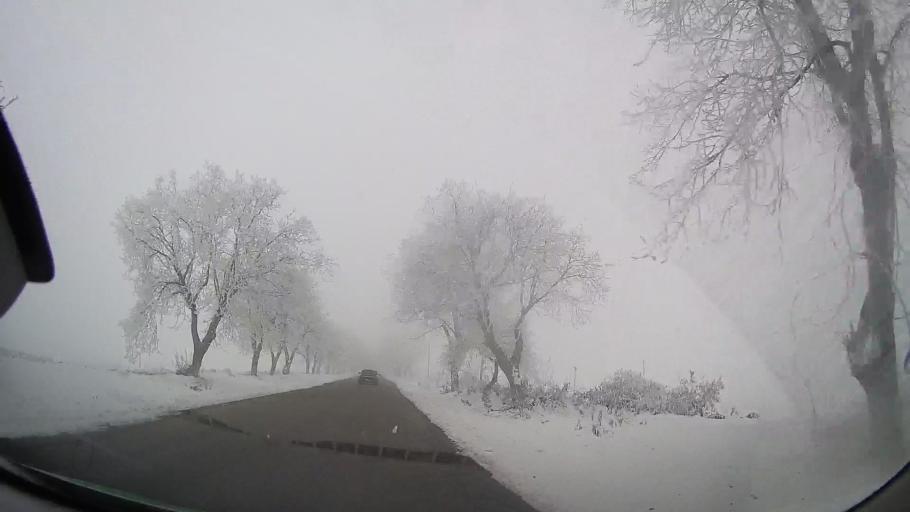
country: RO
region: Neamt
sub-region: Comuna Sabaoani
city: Sabaoani
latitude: 46.9849
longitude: 26.8642
